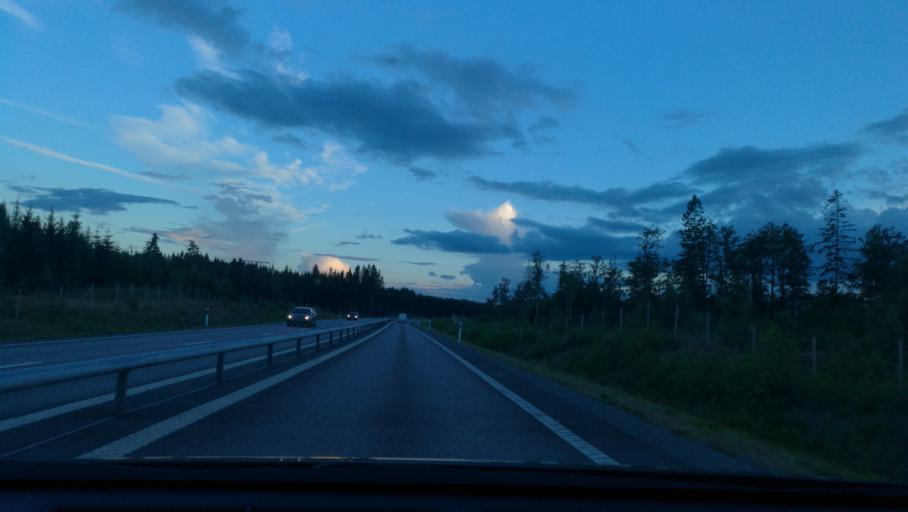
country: SE
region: Soedermanland
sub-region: Katrineholms Kommun
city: Katrineholm
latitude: 58.9489
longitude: 16.2176
